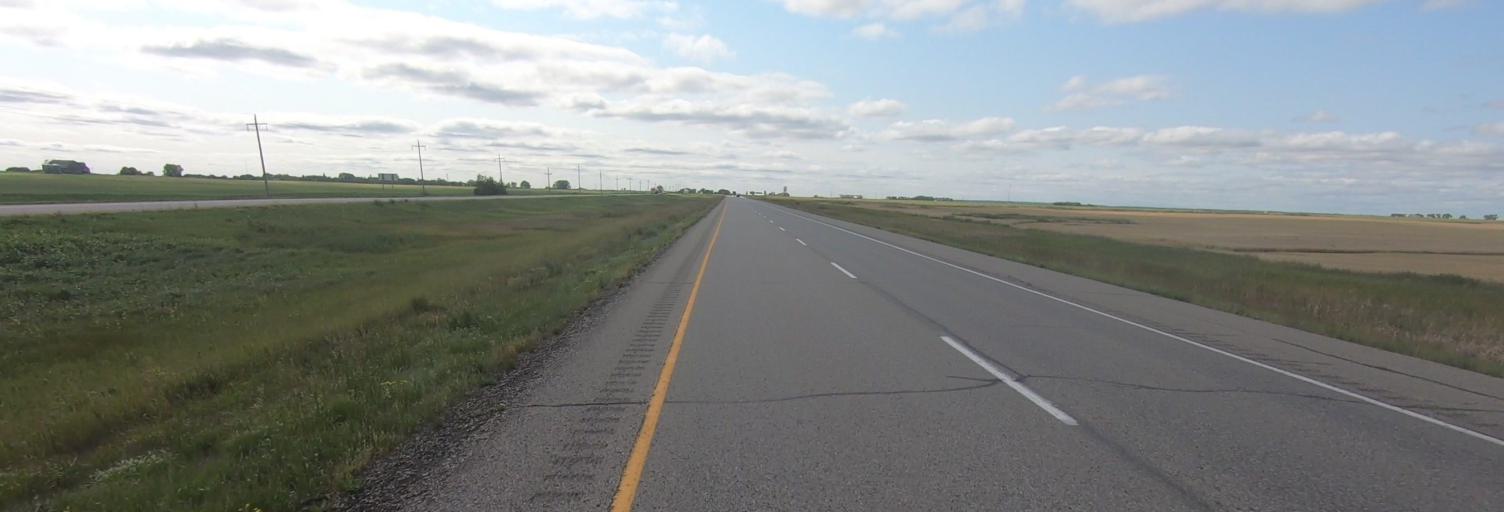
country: CA
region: Manitoba
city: Souris
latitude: 49.7832
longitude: -100.4454
